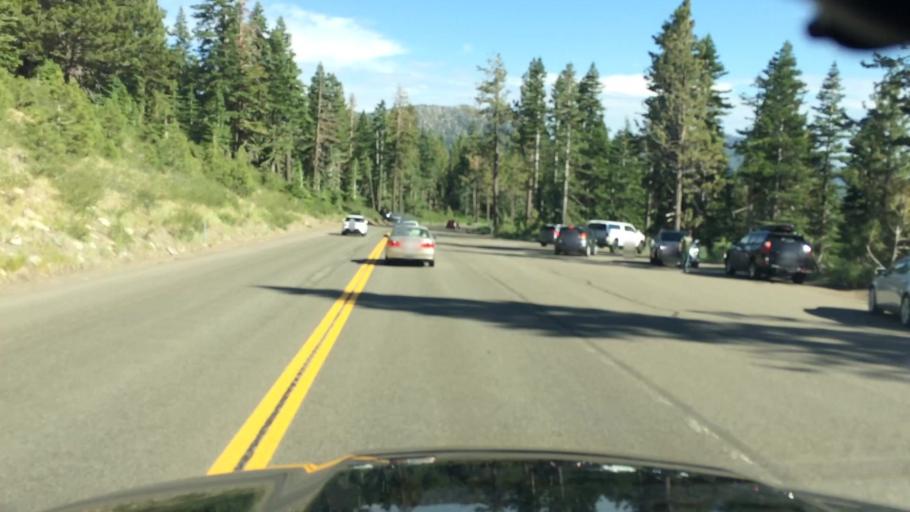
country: US
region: Nevada
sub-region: Washoe County
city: Incline Village
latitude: 39.2687
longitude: -119.9310
